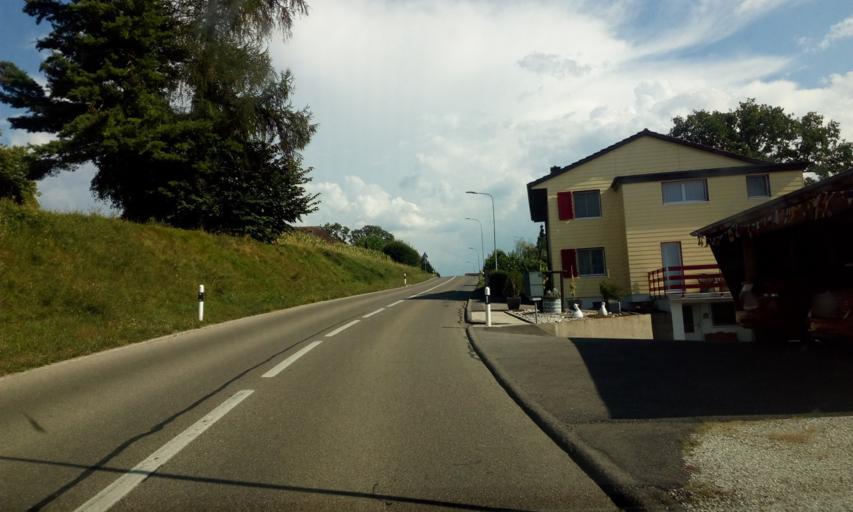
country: CH
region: Fribourg
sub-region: Broye District
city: Domdidier
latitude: 46.9167
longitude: 6.9664
